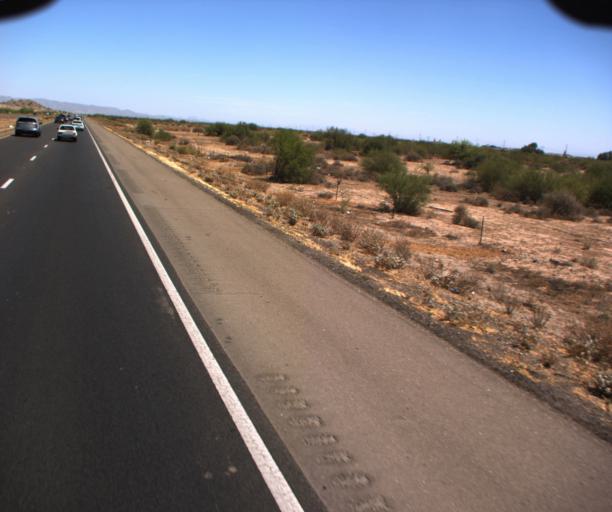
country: US
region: Arizona
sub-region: Pinal County
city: Maricopa
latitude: 33.1524
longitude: -112.0073
